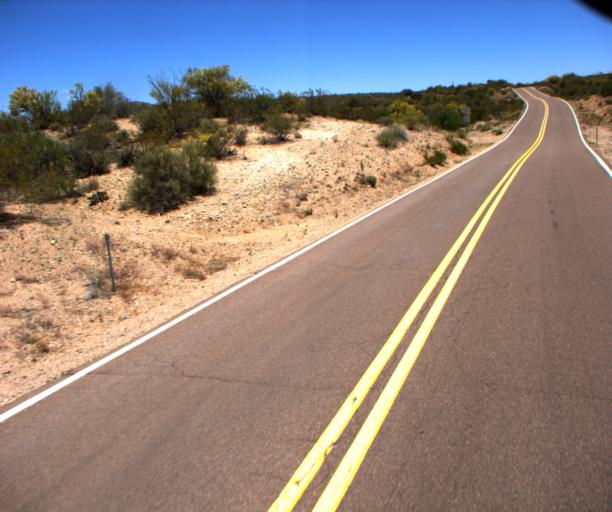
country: US
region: Arizona
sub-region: Yavapai County
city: Bagdad
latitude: 34.4762
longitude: -113.2085
